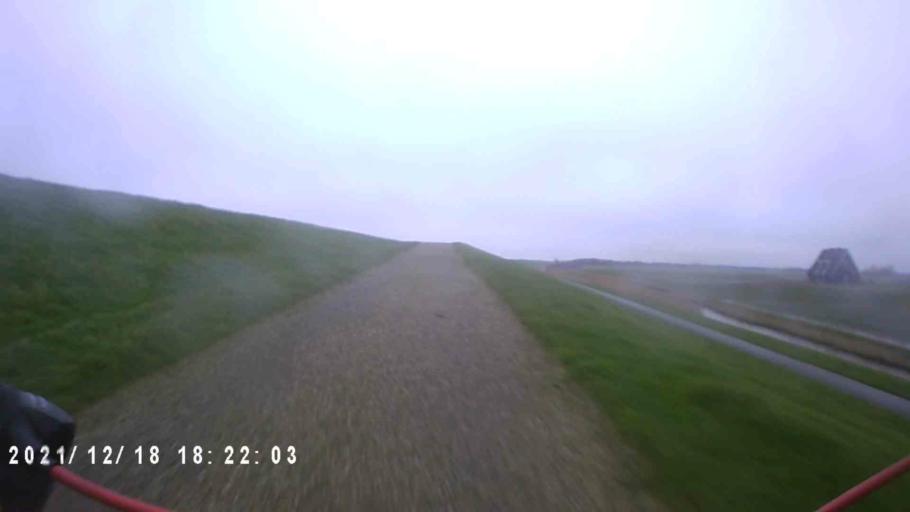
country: NL
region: Friesland
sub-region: Gemeente Dongeradeel
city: Ternaard
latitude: 53.3963
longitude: 5.9873
